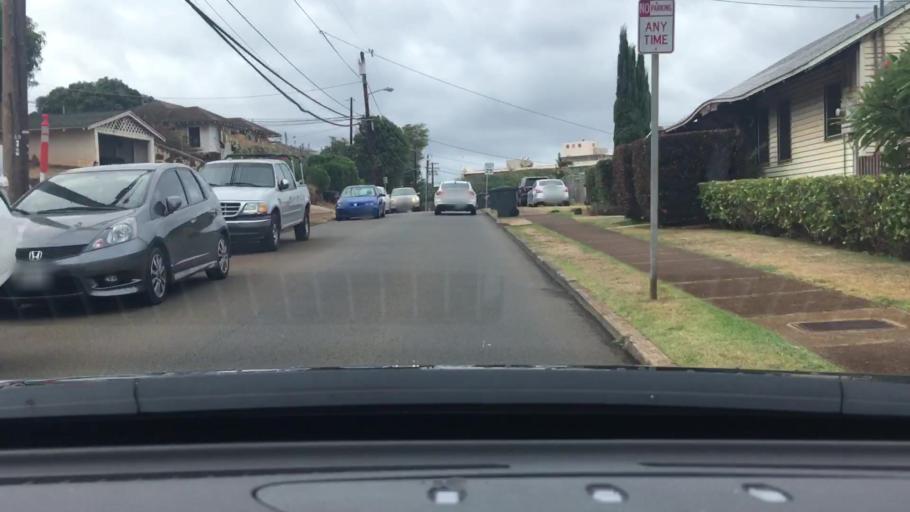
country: US
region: Hawaii
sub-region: Honolulu County
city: Honolulu
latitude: 21.2765
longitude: -157.8022
